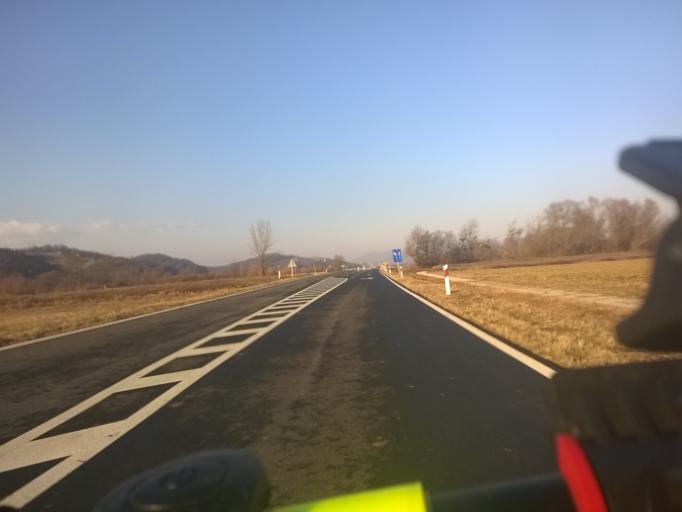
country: HR
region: Krapinsko-Zagorska
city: Zabok
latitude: 46.0442
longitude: 15.9148
